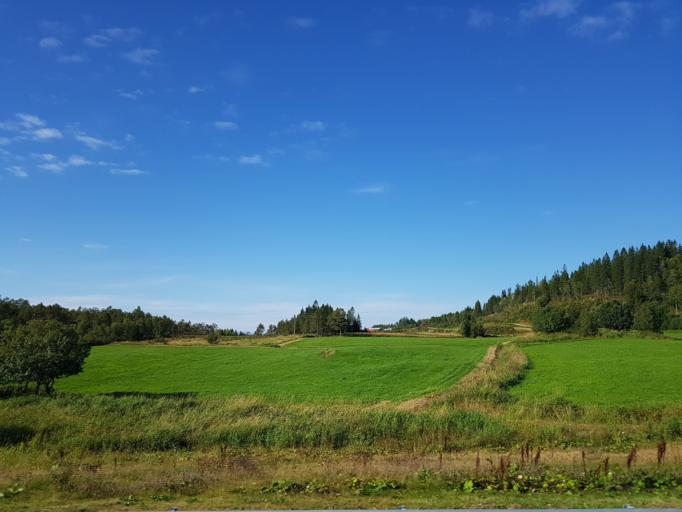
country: NO
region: Sor-Trondelag
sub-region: Trondheim
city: Trondheim
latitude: 63.6466
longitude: 10.2666
